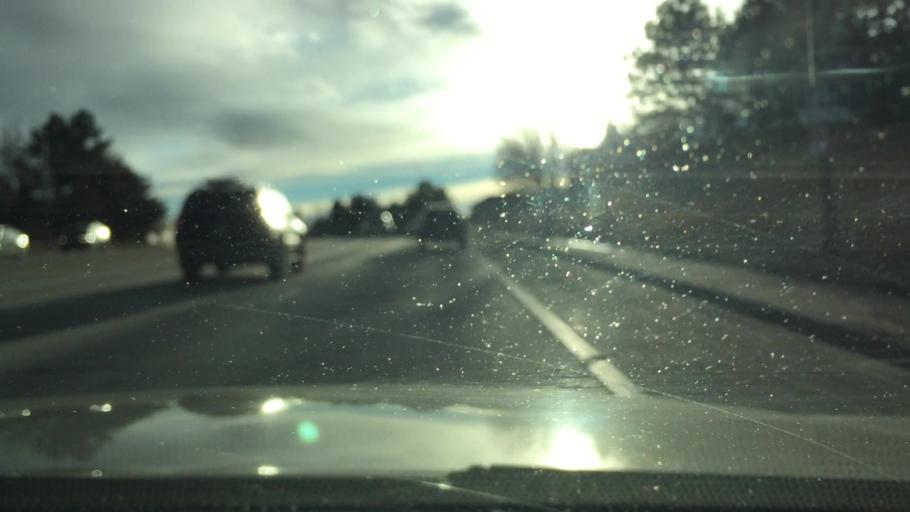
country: US
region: Colorado
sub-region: Douglas County
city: Highlands Ranch
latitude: 39.5399
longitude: -104.9597
